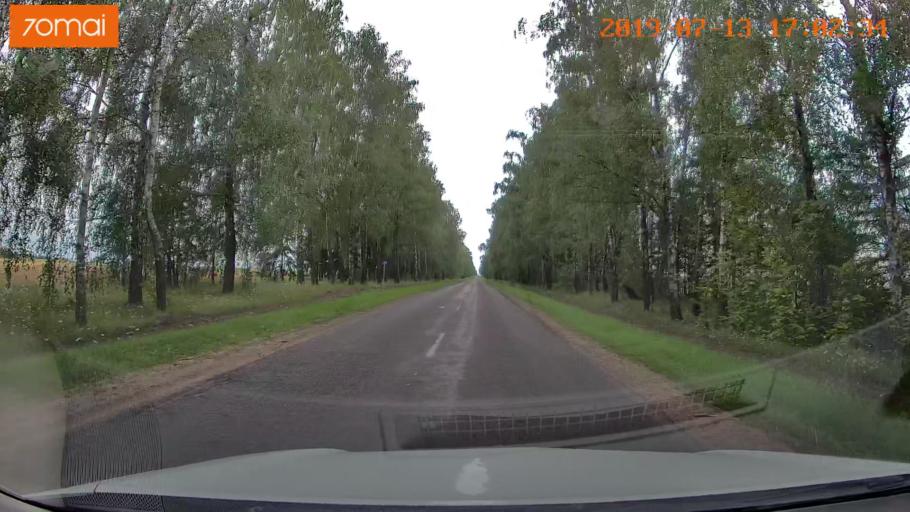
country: BY
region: Mogilev
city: Kirawsk
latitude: 53.2847
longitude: 29.3857
